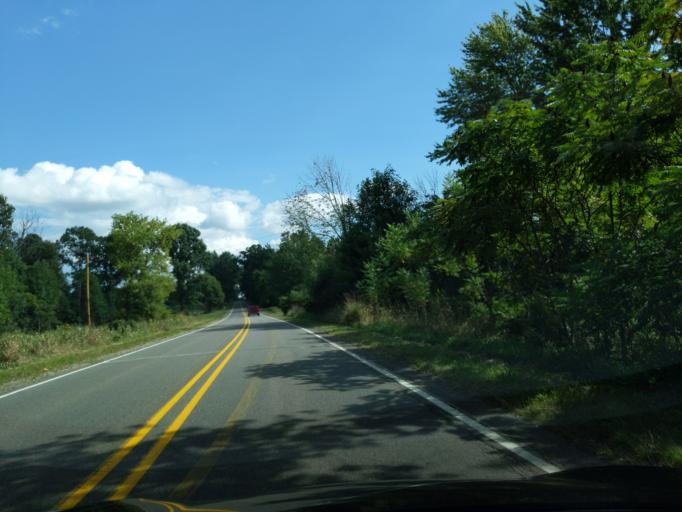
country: US
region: Michigan
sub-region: Jackson County
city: Jackson
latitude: 42.2855
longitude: -84.4605
